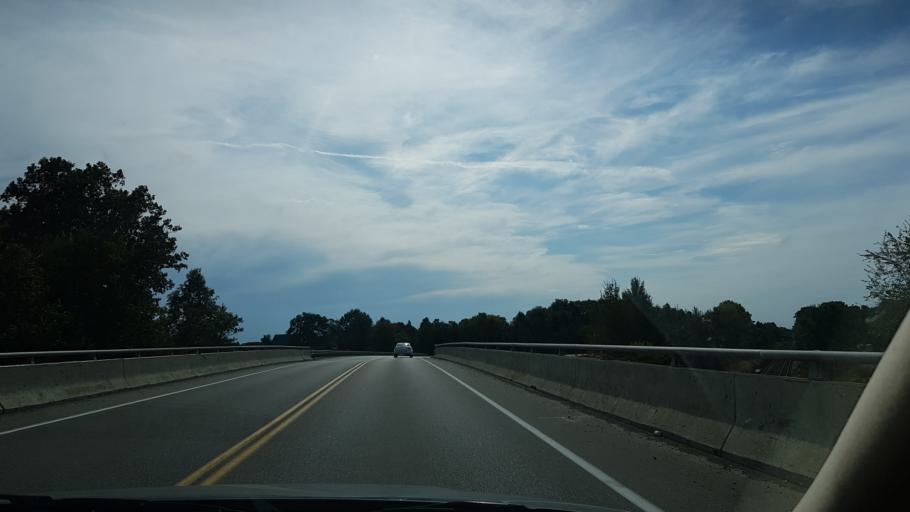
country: CA
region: Ontario
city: Delaware
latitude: 42.9721
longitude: -81.3933
